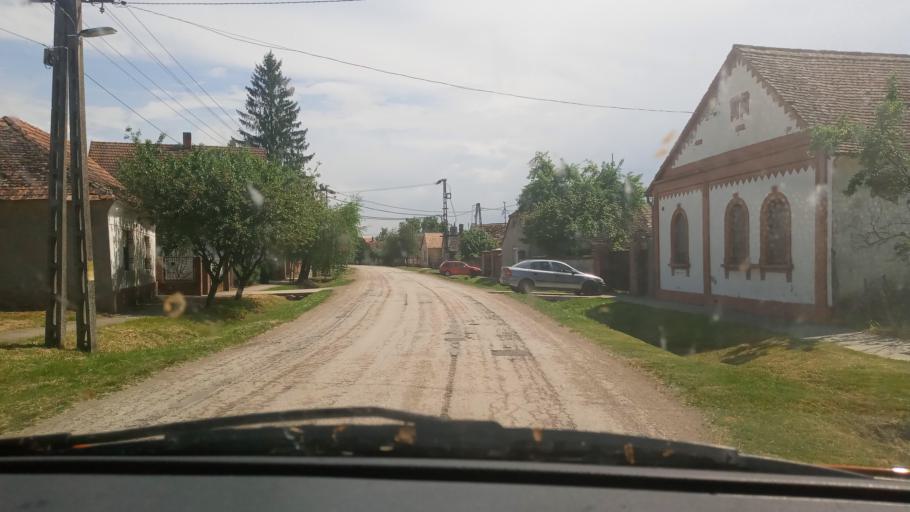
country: HU
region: Baranya
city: Beremend
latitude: 45.7912
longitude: 18.3506
